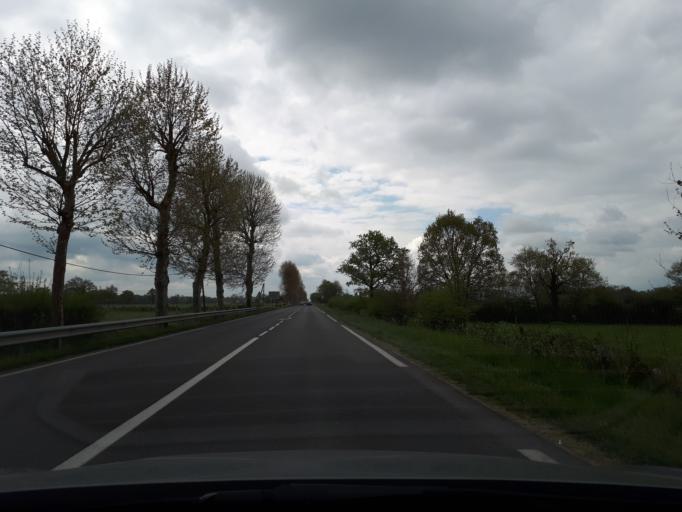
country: FR
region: Rhone-Alpes
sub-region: Departement de la Loire
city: Feurs
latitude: 45.7148
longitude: 4.2265
